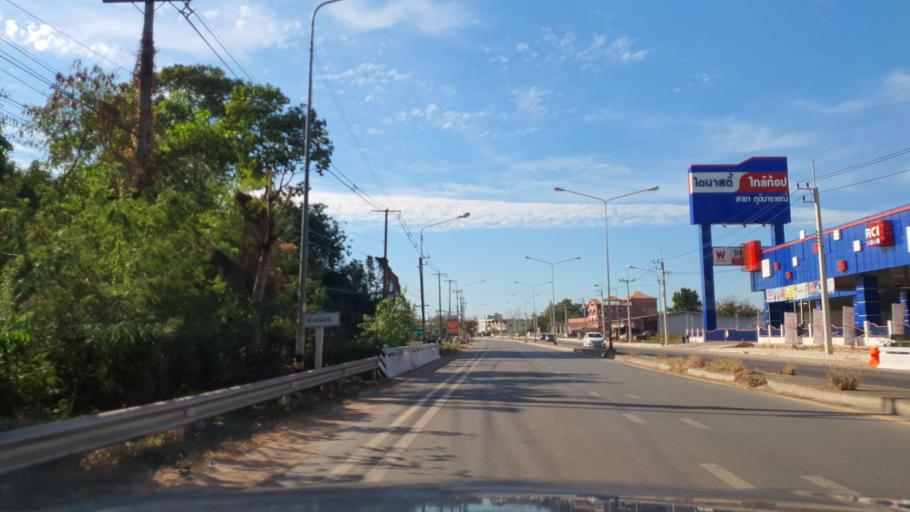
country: TH
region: Kalasin
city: Kuchinarai
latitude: 16.5369
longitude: 104.0653
